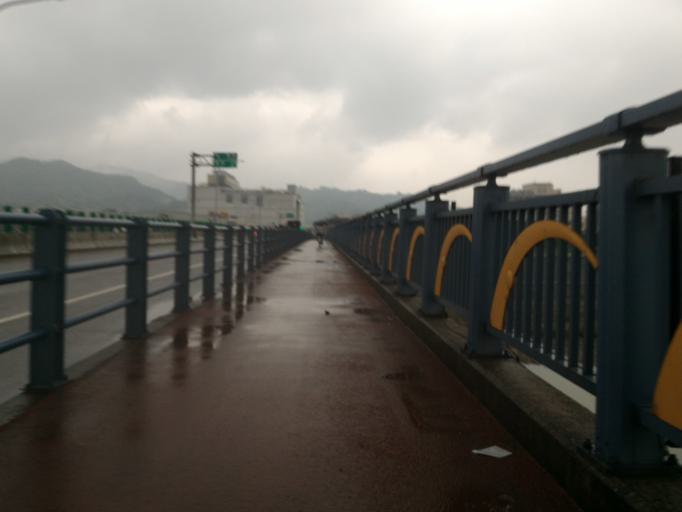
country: TW
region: Taipei
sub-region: Taipei
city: Banqiao
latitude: 24.9677
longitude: 121.4047
